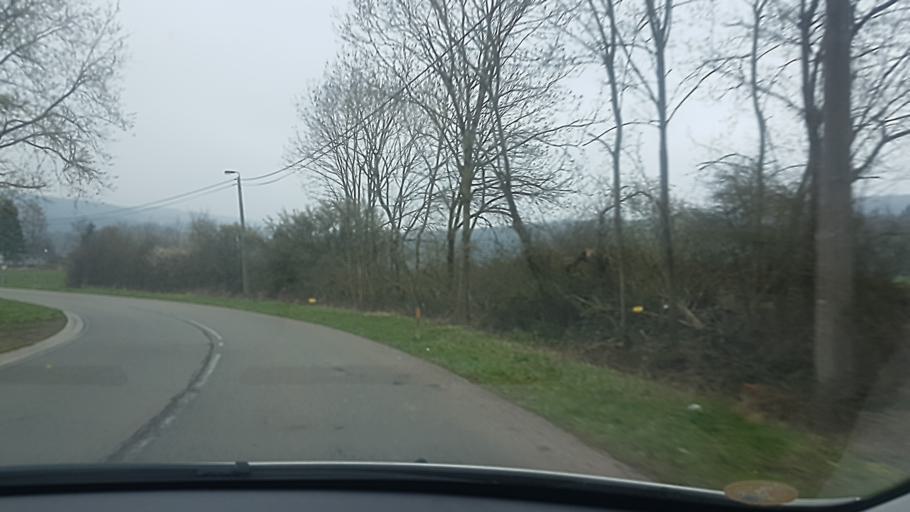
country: BE
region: Wallonia
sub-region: Province de Namur
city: Couvin
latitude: 50.0638
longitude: 4.6075
